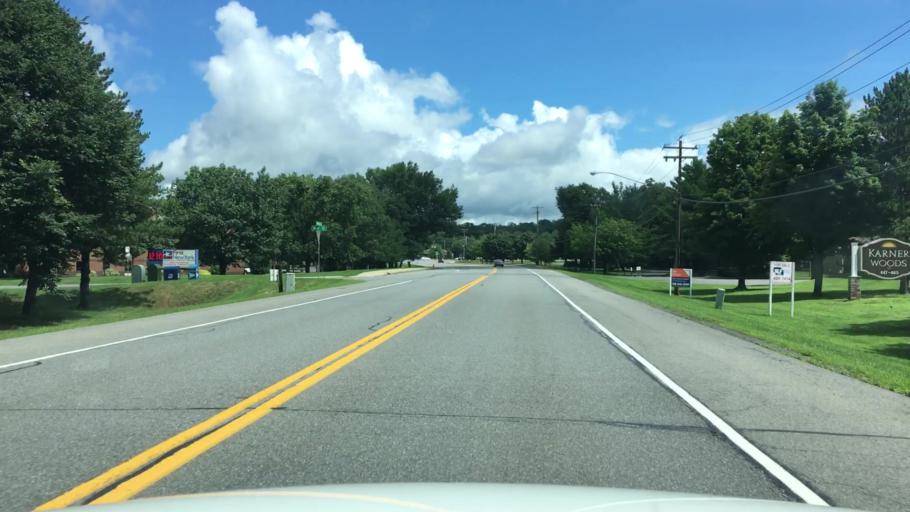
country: US
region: New York
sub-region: Albany County
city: Colonie
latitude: 42.7409
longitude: -73.8414
